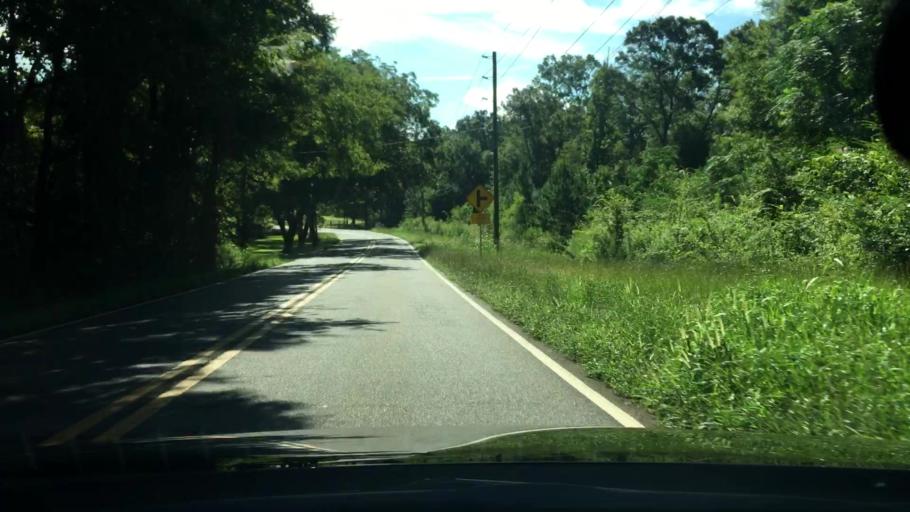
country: US
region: Georgia
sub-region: Putnam County
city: Jefferson
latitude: 33.4386
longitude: -83.3353
